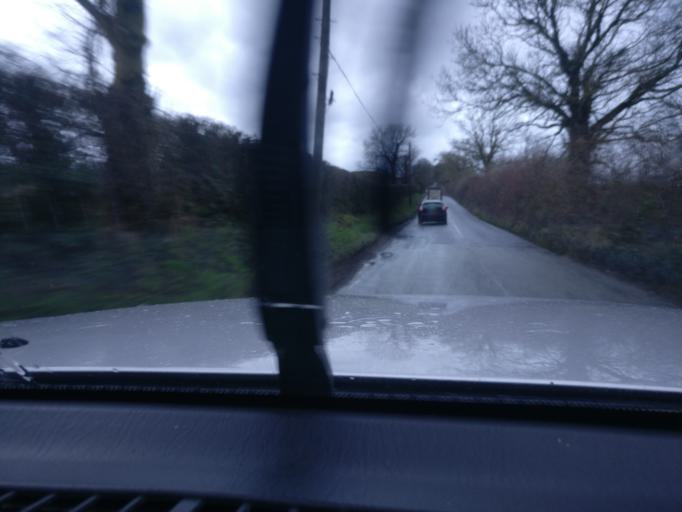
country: IE
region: Leinster
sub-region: An Mhi
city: Longwood
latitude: 53.4410
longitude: -6.9835
